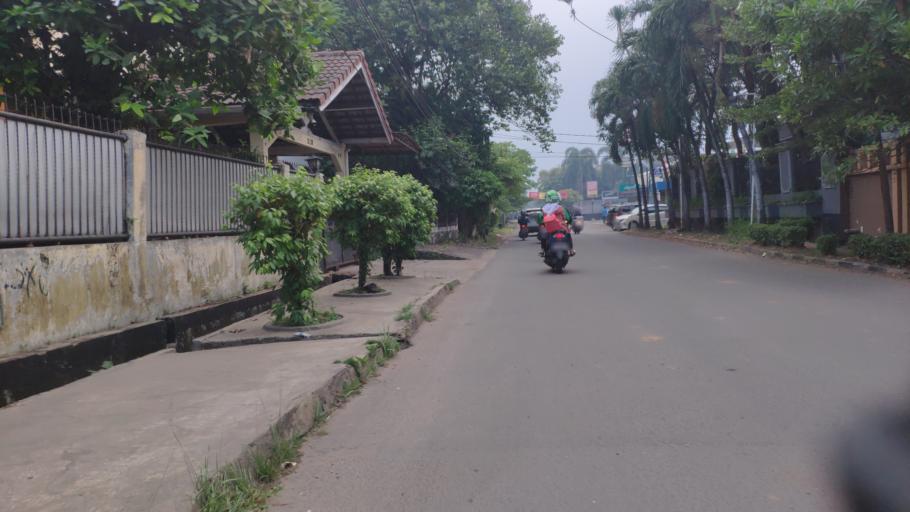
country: ID
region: West Java
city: Pamulang
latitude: -6.3465
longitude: 106.7793
